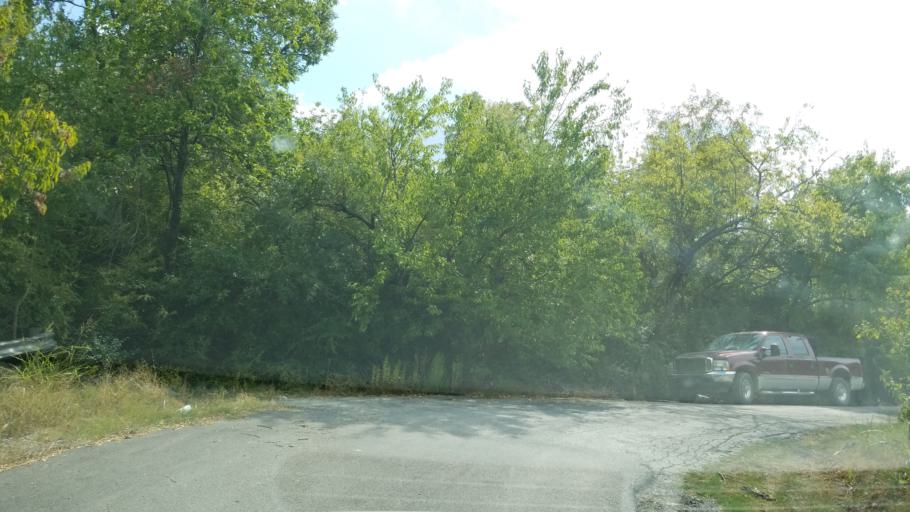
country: US
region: Texas
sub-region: Dallas County
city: Cockrell Hill
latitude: 32.7704
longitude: -96.8549
